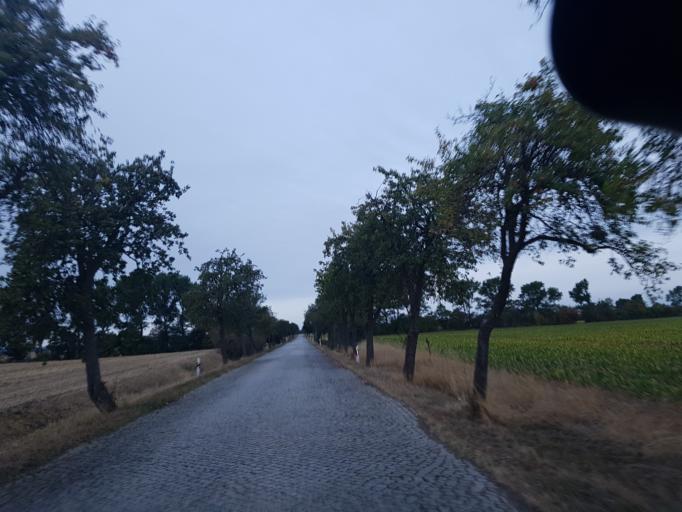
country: DE
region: Brandenburg
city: Muhlberg
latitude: 51.4954
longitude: 13.2157
